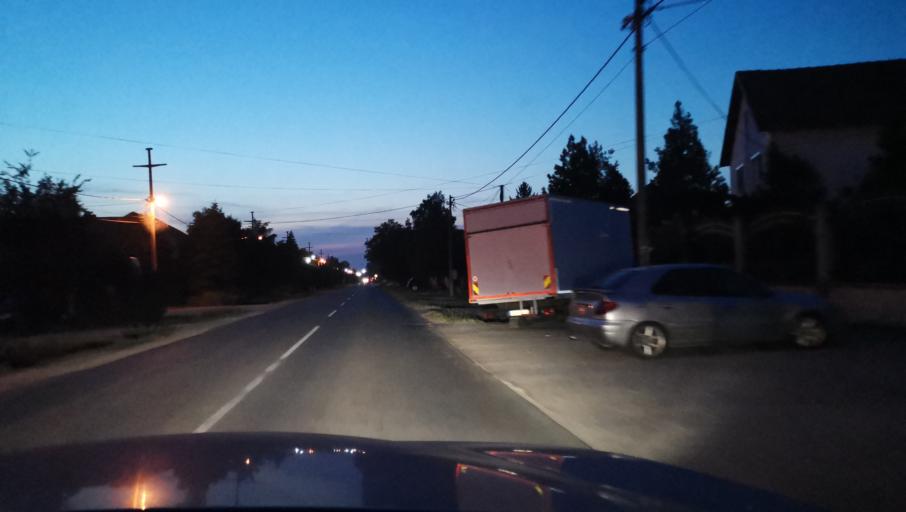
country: RS
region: Central Serbia
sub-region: Belgrade
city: Surcin
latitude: 44.7599
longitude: 20.2547
